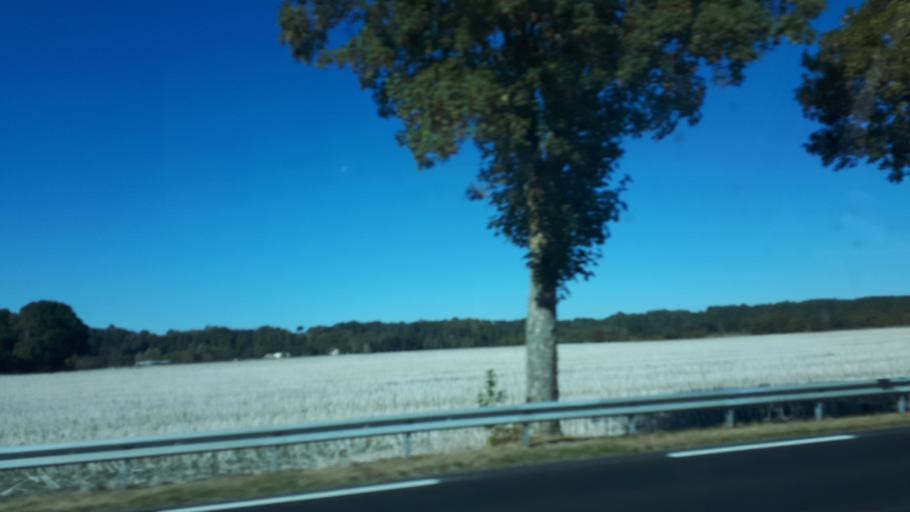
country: FR
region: Centre
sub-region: Departement d'Eure-et-Loir
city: Marboue
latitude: 48.1036
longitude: 1.3300
